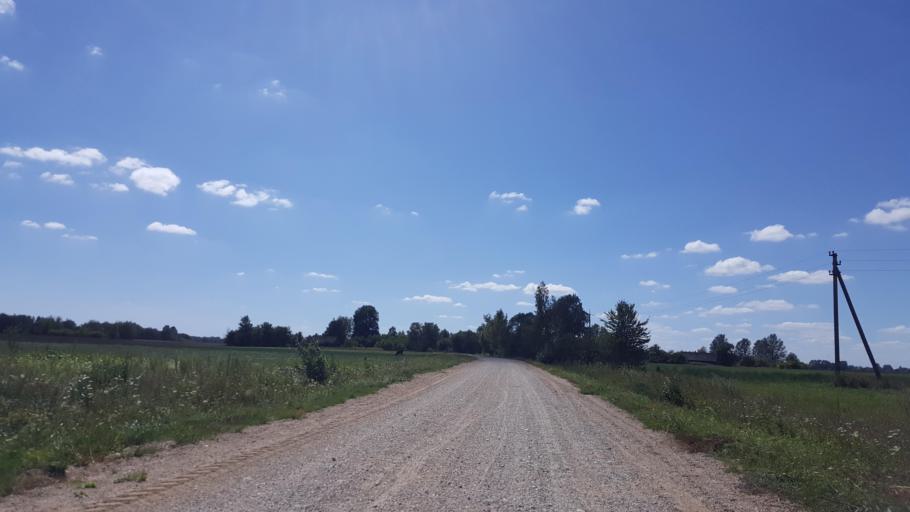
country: BY
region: Brest
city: Horad Kobryn
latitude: 52.3148
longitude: 24.3924
